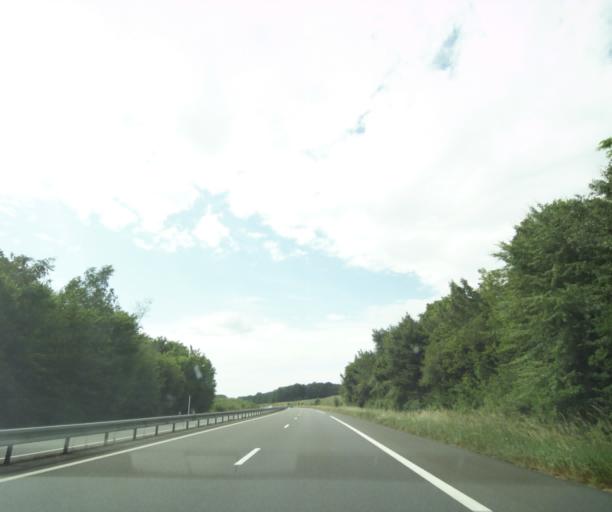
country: FR
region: Pays de la Loire
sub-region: Departement de Maine-et-Loire
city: Brion
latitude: 47.4274
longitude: -0.1474
